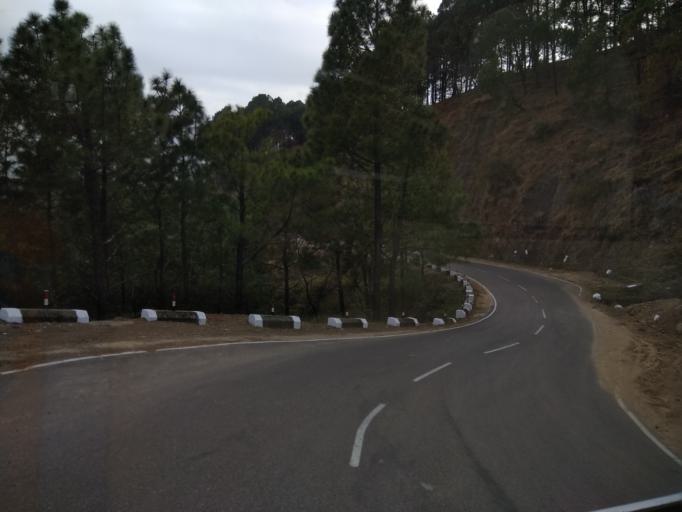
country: IN
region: Himachal Pradesh
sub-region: Kangra
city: Palampur
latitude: 32.1140
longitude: 76.4887
